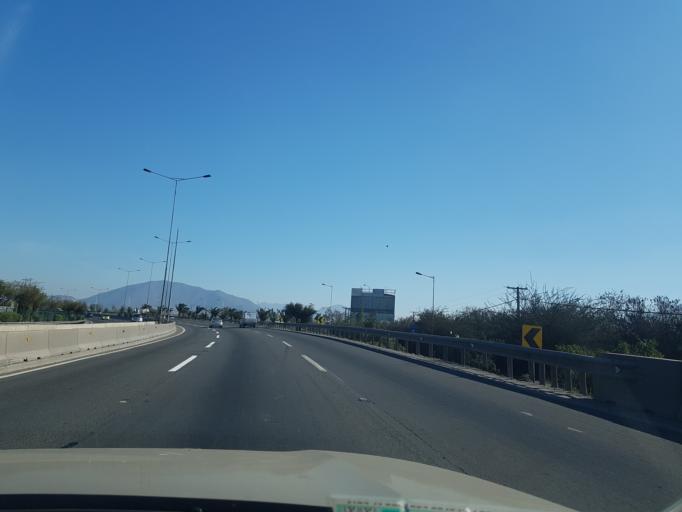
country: CL
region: Santiago Metropolitan
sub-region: Provincia de Santiago
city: Lo Prado
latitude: -33.4041
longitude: -70.7812
